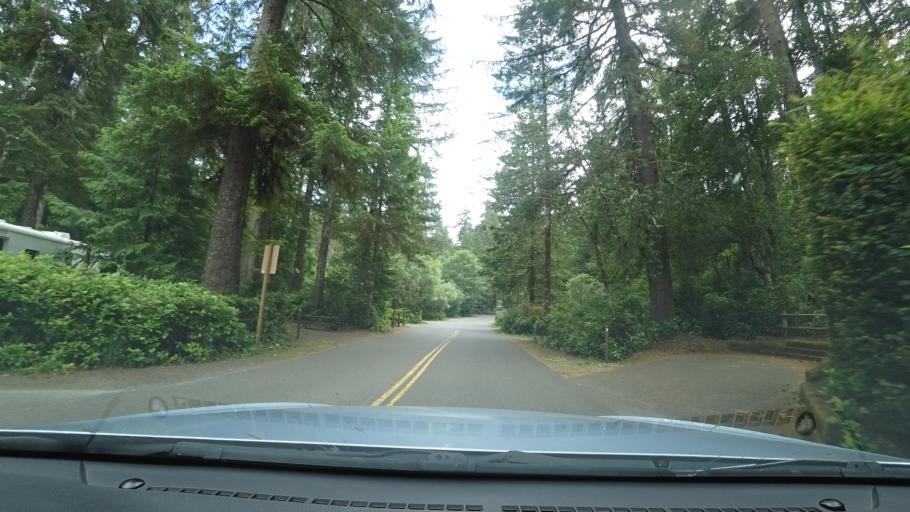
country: US
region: Oregon
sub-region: Lane County
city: Dunes City
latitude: 43.9255
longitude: -124.1119
